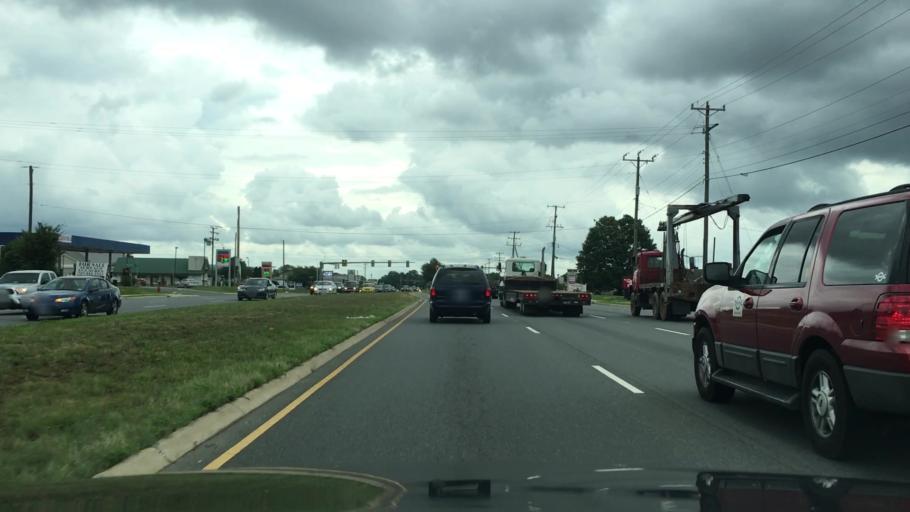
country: US
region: Virginia
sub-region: Stafford County
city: Falmouth
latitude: 38.2890
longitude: -77.5408
